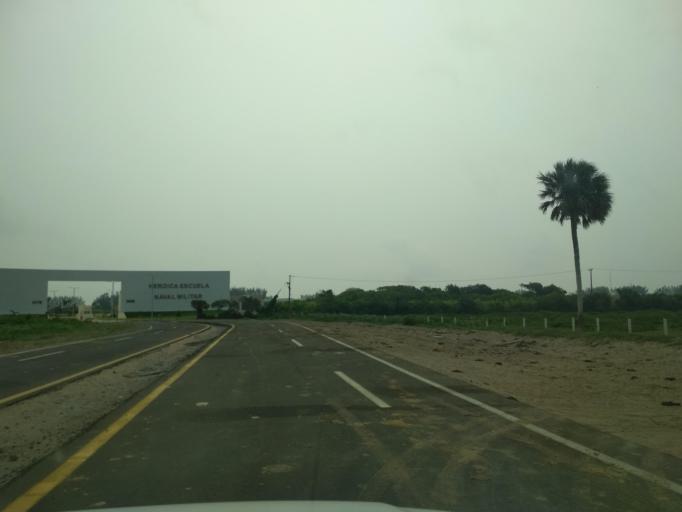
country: MX
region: Veracruz
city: Anton Lizardo
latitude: 19.0464
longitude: -95.9792
